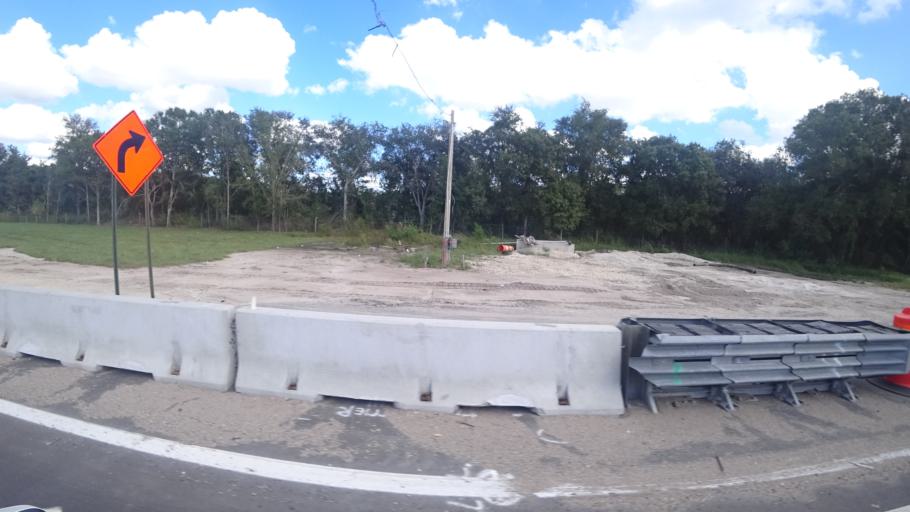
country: US
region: Florida
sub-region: Sarasota County
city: Desoto Lakes
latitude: 27.4438
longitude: -82.4582
